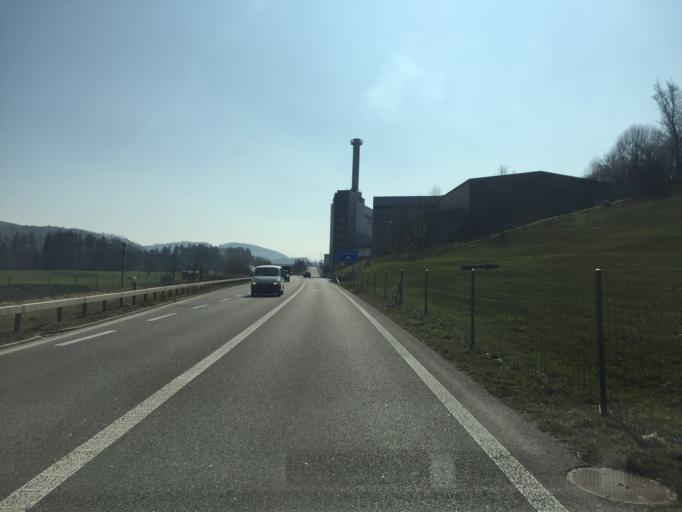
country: CH
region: Saint Gallen
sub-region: Wahlkreis Wil
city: Jonschwil
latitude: 47.4256
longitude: 9.0672
